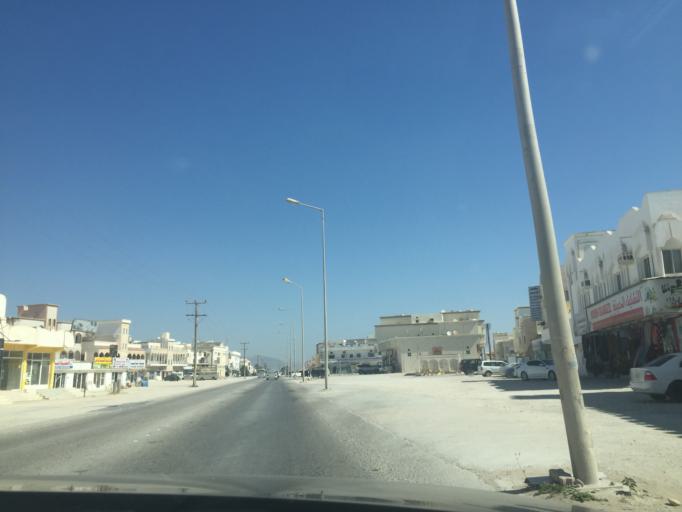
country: OM
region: Zufar
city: Salalah
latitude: 17.0209
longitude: 54.1629
